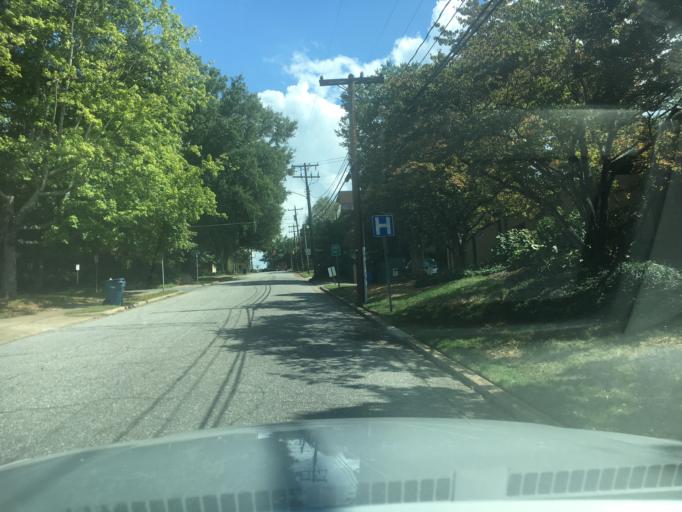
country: US
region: North Carolina
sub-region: Catawba County
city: Hickory
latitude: 35.7385
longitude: -81.3394
